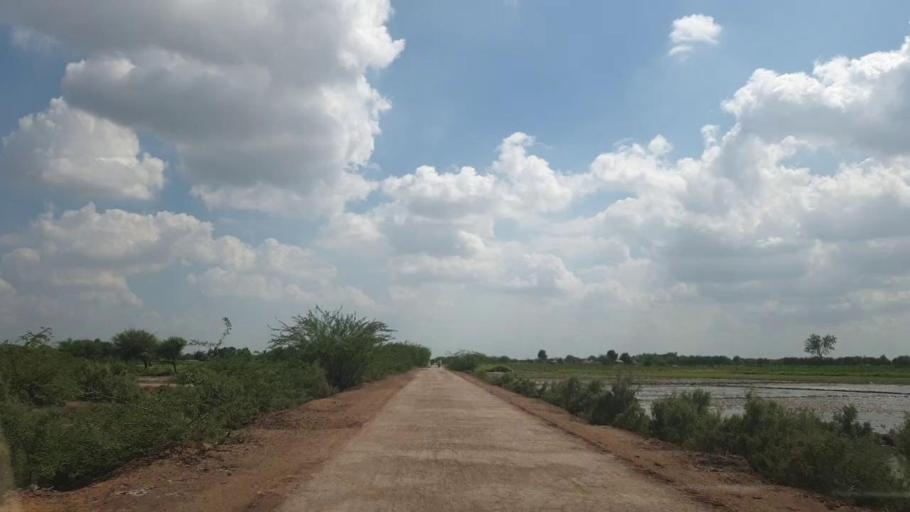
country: PK
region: Sindh
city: Pithoro
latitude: 25.6021
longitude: 69.4054
